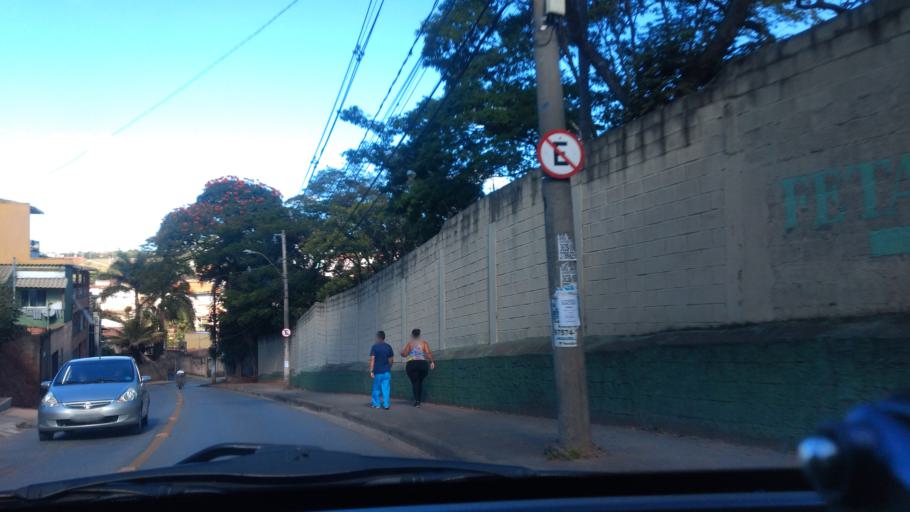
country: BR
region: Minas Gerais
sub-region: Santa Luzia
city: Santa Luzia
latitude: -19.8117
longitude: -43.9452
